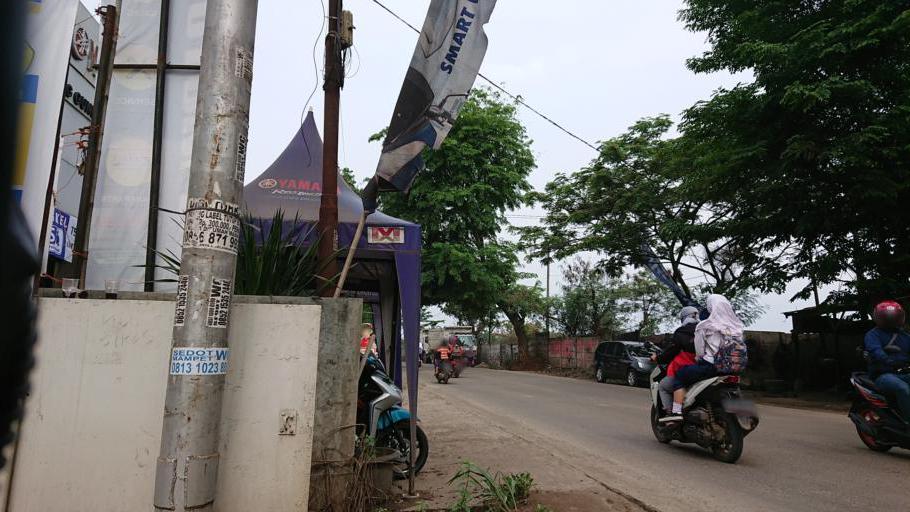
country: ID
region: West Java
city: Parung
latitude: -6.3841
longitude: 106.6827
